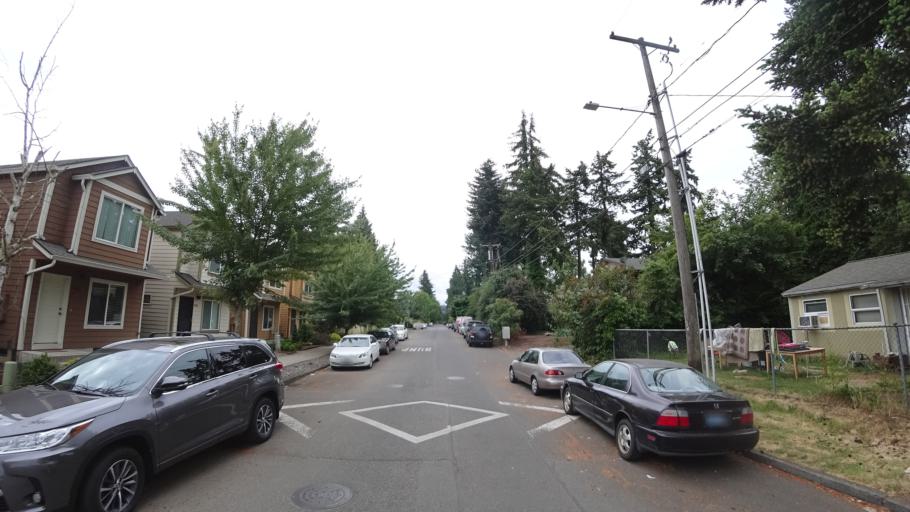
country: US
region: Oregon
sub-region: Multnomah County
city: Lents
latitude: 45.5037
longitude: -122.5493
